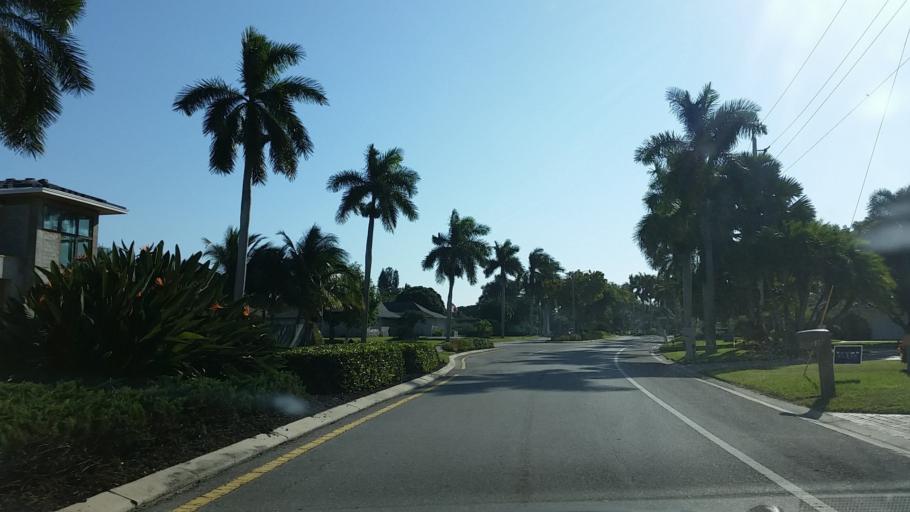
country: US
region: Florida
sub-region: Collier County
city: Naples
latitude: 26.1810
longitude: -81.8064
